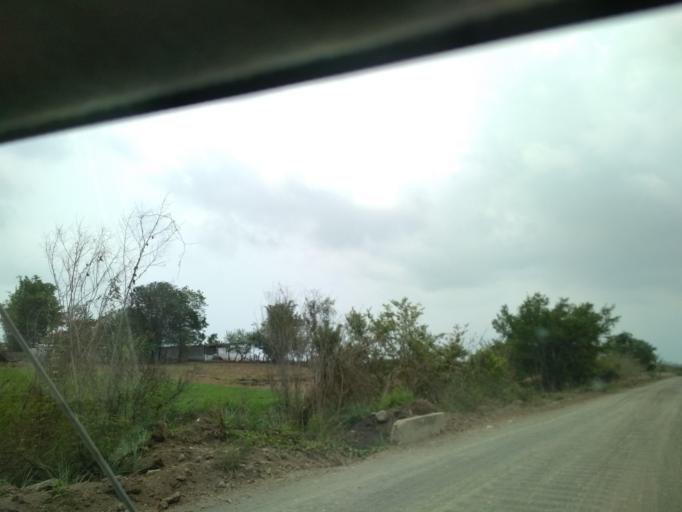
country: MX
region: Veracruz
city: Paso del Toro
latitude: 19.0172
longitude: -96.1348
